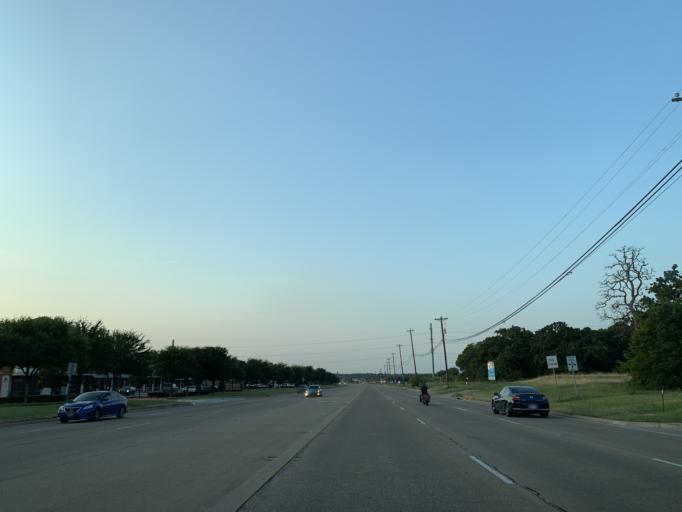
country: US
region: Texas
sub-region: Tarrant County
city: Keller
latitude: 32.9172
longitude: -97.2550
